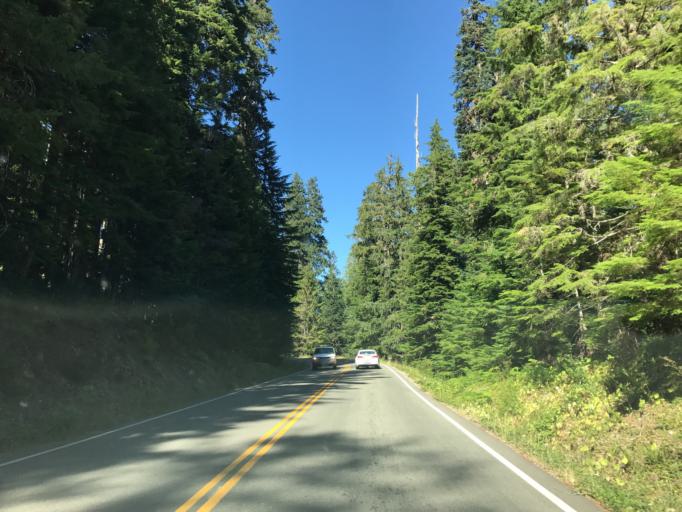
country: US
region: Washington
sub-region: Pierce County
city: Buckley
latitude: 46.7454
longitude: -121.5729
